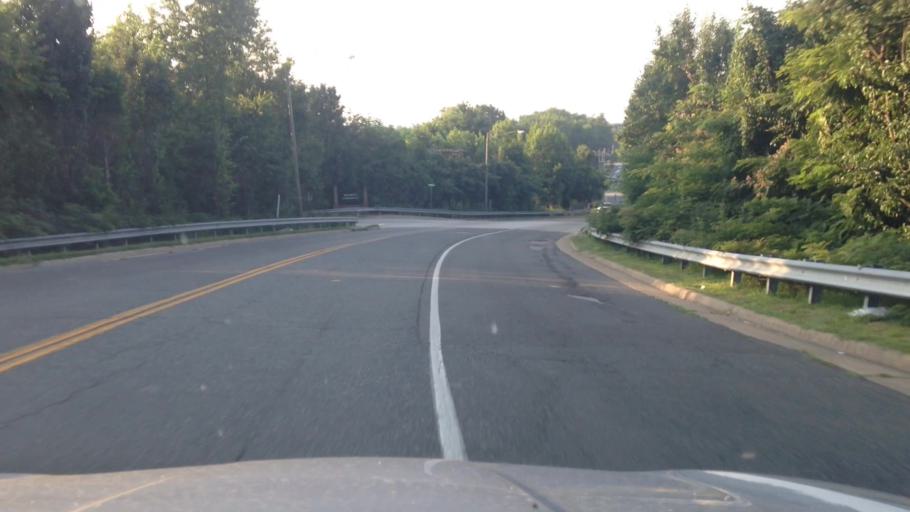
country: US
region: Virginia
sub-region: Prince William County
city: Woodbridge
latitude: 38.6567
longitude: -77.2479
